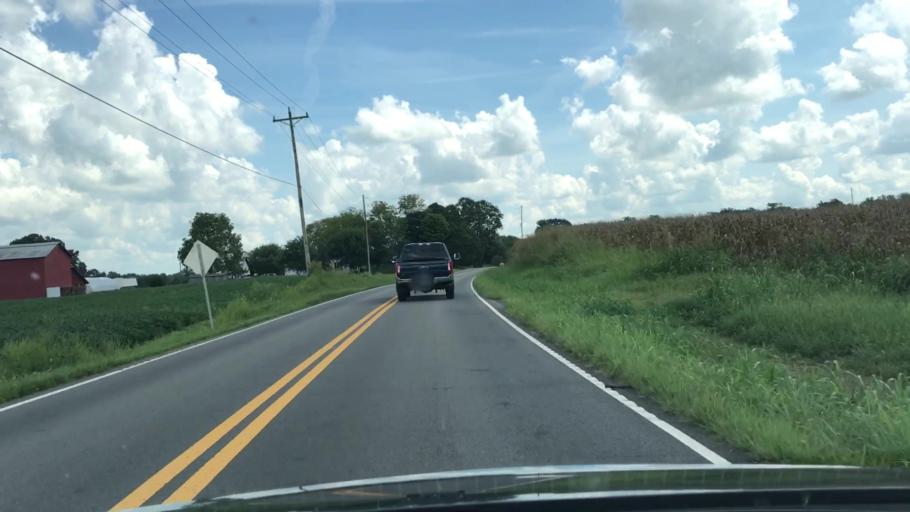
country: US
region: Tennessee
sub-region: Robertson County
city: Springfield
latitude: 36.5549
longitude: -86.8188
